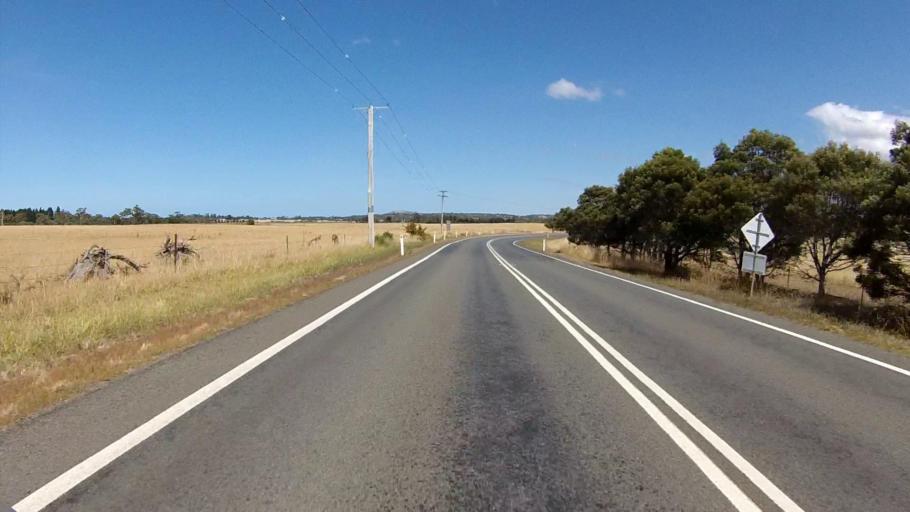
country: AU
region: Tasmania
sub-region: Break O'Day
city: St Helens
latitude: -42.1004
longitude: 148.0627
